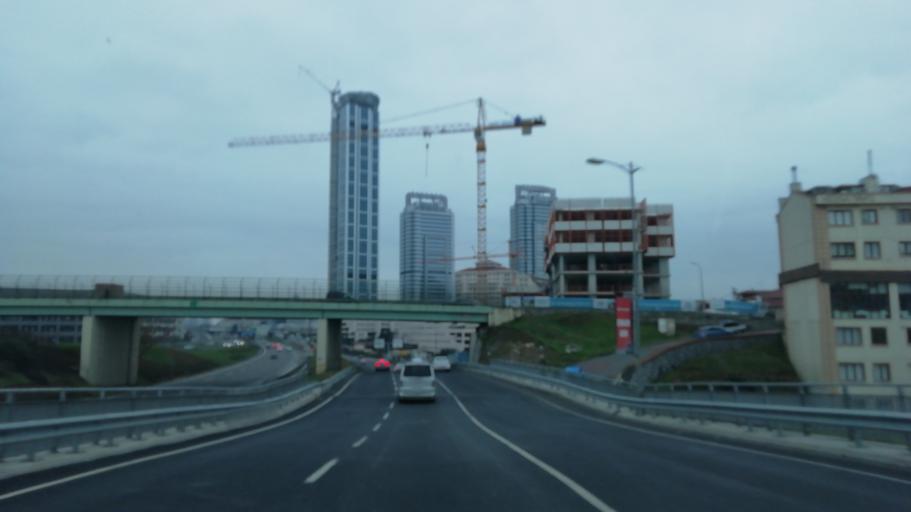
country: TR
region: Istanbul
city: UEskuedar
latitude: 41.0064
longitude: 29.0647
